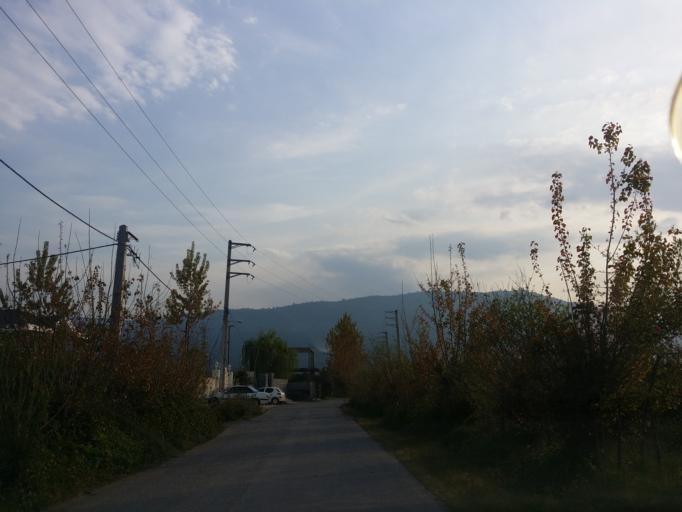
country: IR
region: Mazandaran
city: Chalus
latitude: 36.6769
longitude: 51.3728
